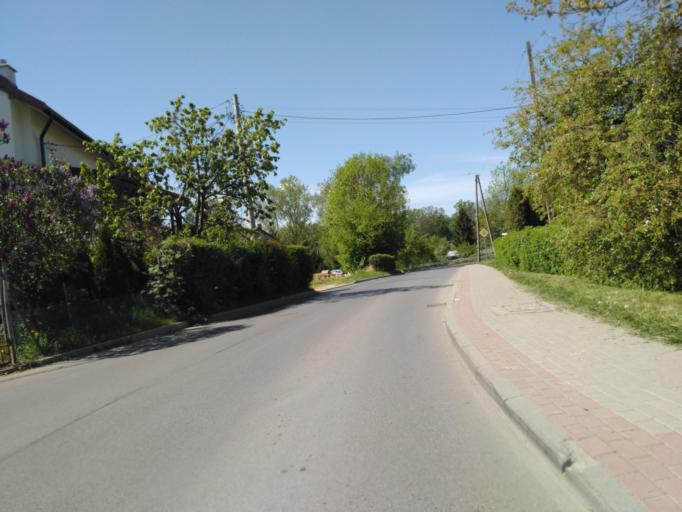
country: PL
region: Subcarpathian Voivodeship
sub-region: Krosno
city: Krosno
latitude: 49.6868
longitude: 21.7905
